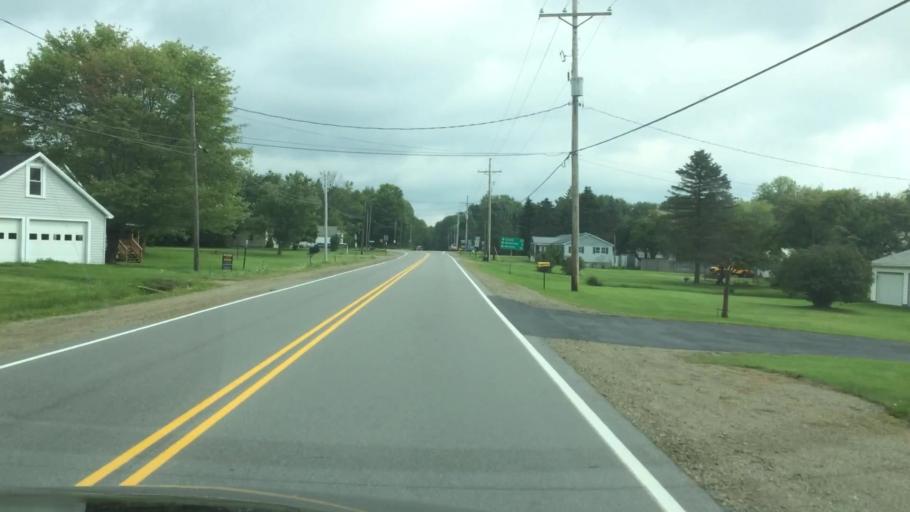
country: US
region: Pennsylvania
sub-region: McKean County
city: Bradford
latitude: 41.8769
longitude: -78.5799
